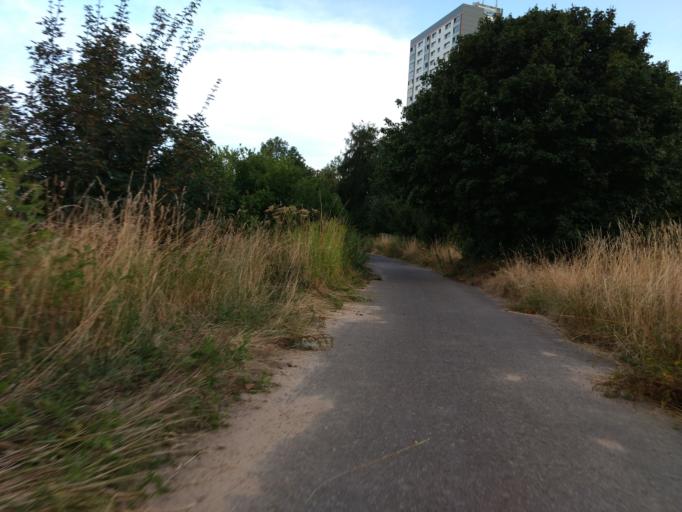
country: DE
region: Saarland
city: Wallerfangen
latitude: 49.3245
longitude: 6.7308
